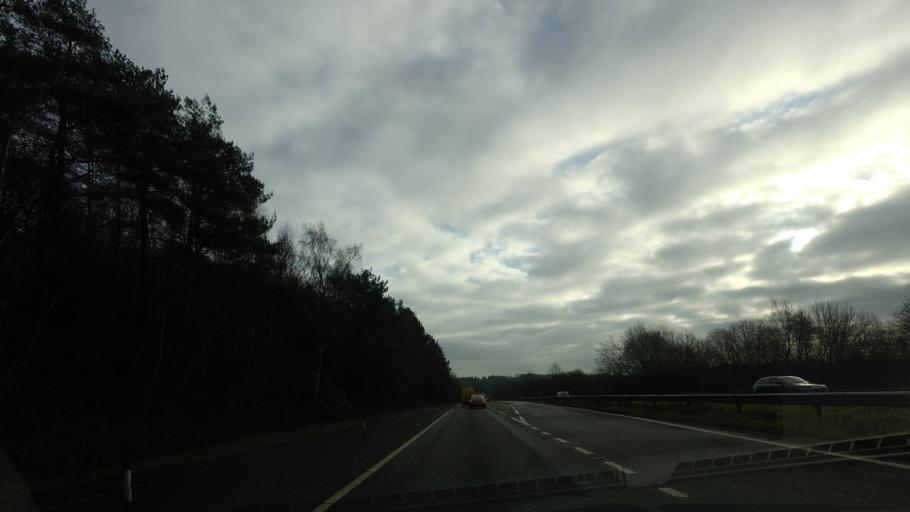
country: GB
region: England
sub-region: Kent
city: Hawkhurst
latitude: 51.0635
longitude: 0.4417
